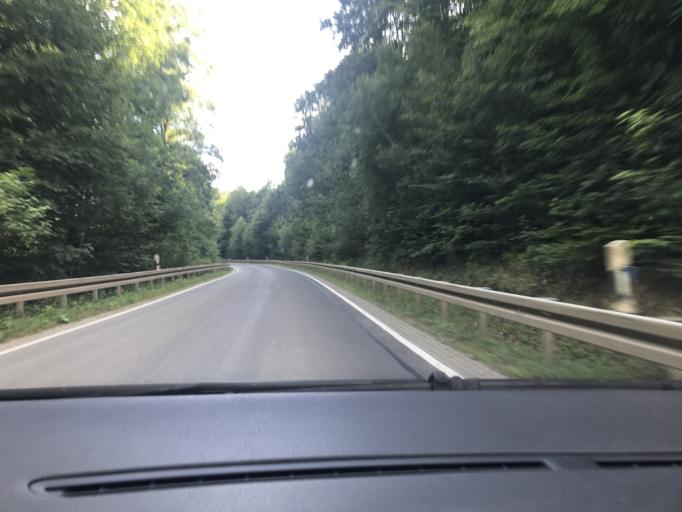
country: DE
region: Thuringia
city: Geisleden
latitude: 51.3718
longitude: 10.1986
